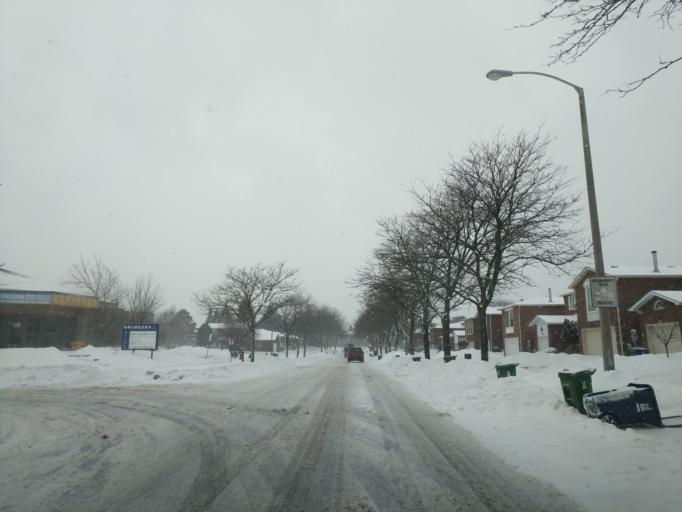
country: CA
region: Ontario
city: Scarborough
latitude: 43.8109
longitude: -79.2803
